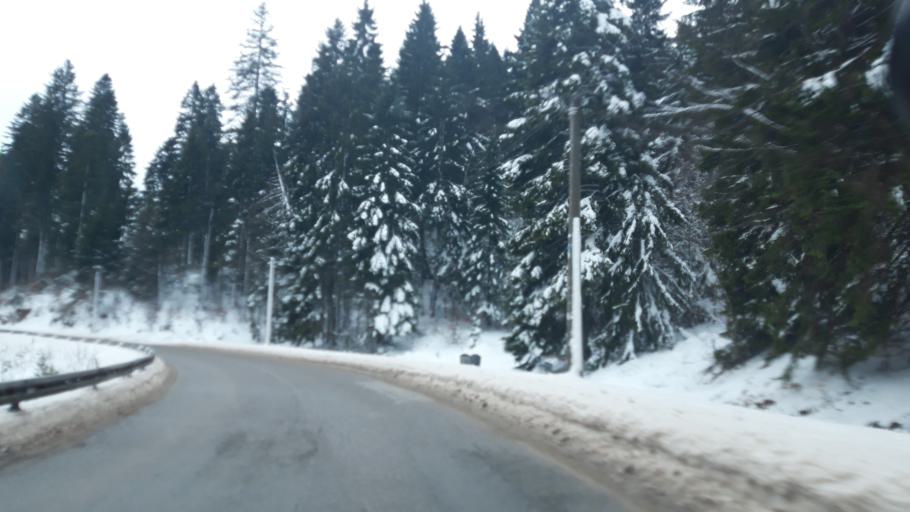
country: BA
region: Republika Srpska
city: Han Pijesak
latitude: 44.0877
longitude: 18.9526
